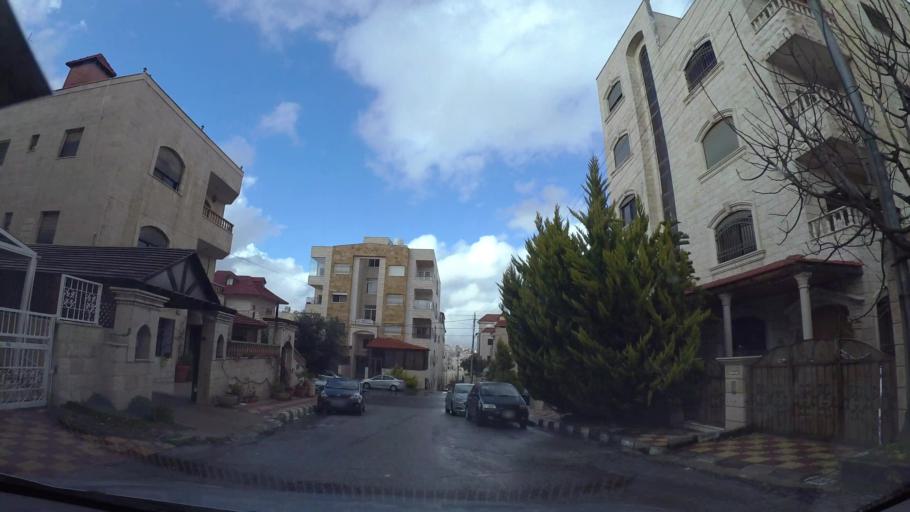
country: JO
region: Amman
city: Al Jubayhah
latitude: 32.0302
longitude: 35.8668
